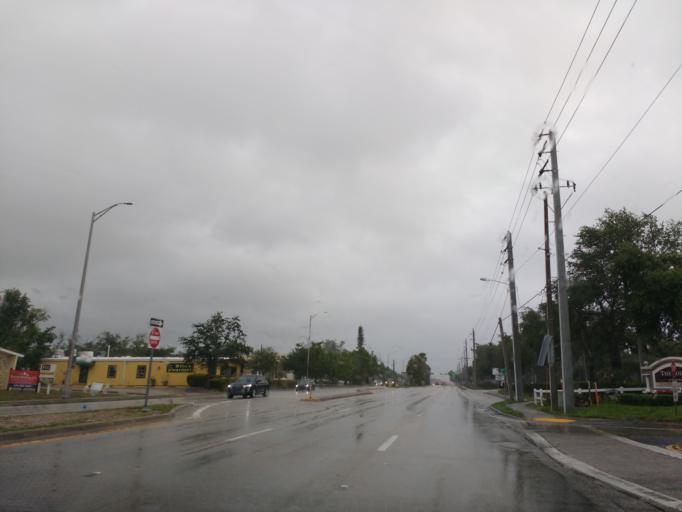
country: US
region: Florida
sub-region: Collier County
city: Naples
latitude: 26.1324
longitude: -81.7663
